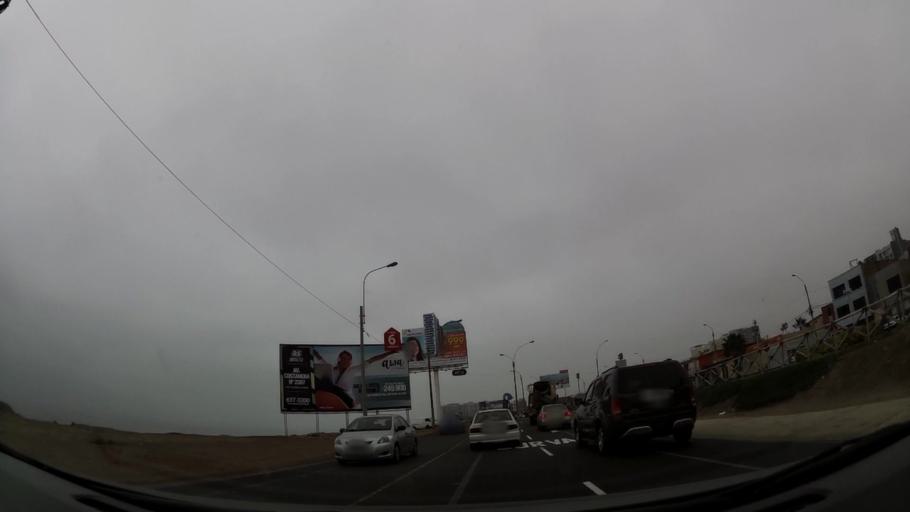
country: PE
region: Callao
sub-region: Callao
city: Callao
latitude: -12.0866
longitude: -77.0950
